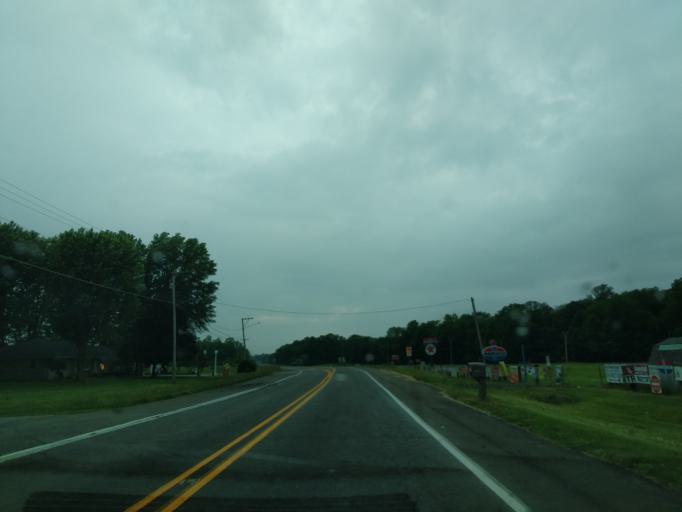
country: US
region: Indiana
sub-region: Madison County
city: Chesterfield
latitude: 40.0914
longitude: -85.6215
